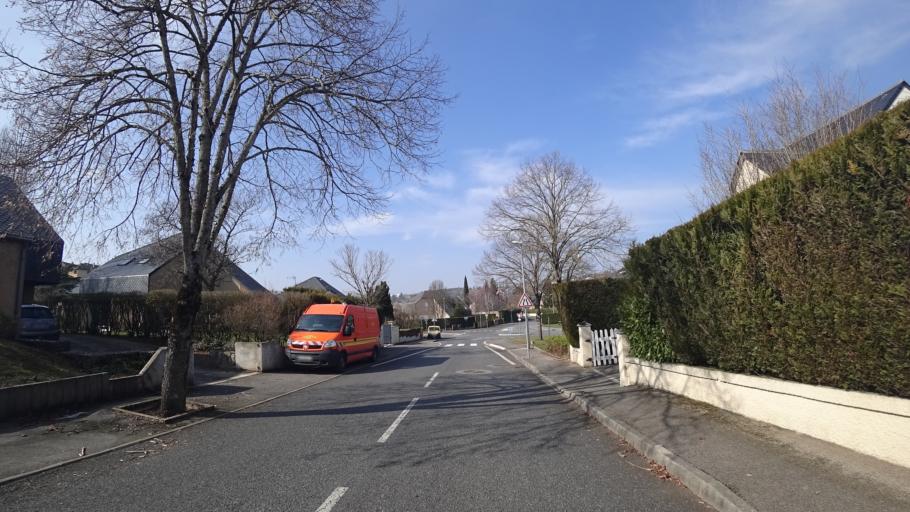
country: FR
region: Midi-Pyrenees
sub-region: Departement de l'Aveyron
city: Rodez
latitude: 44.3646
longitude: 2.5637
